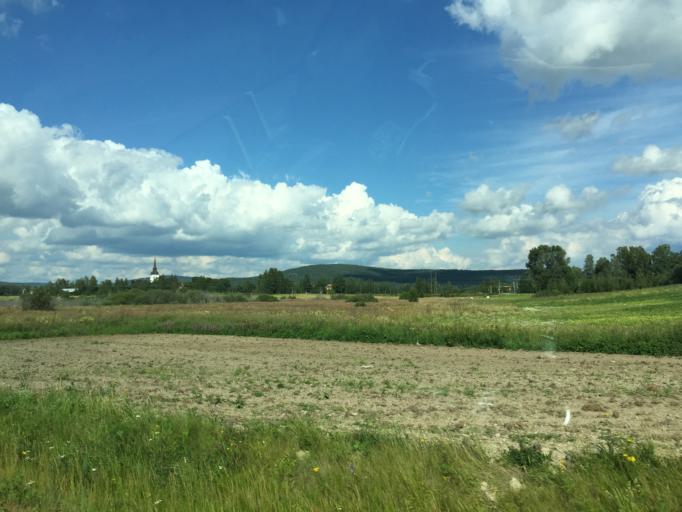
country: SE
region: Gaevleborg
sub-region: Bollnas Kommun
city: Kilafors
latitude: 61.2382
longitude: 16.5518
